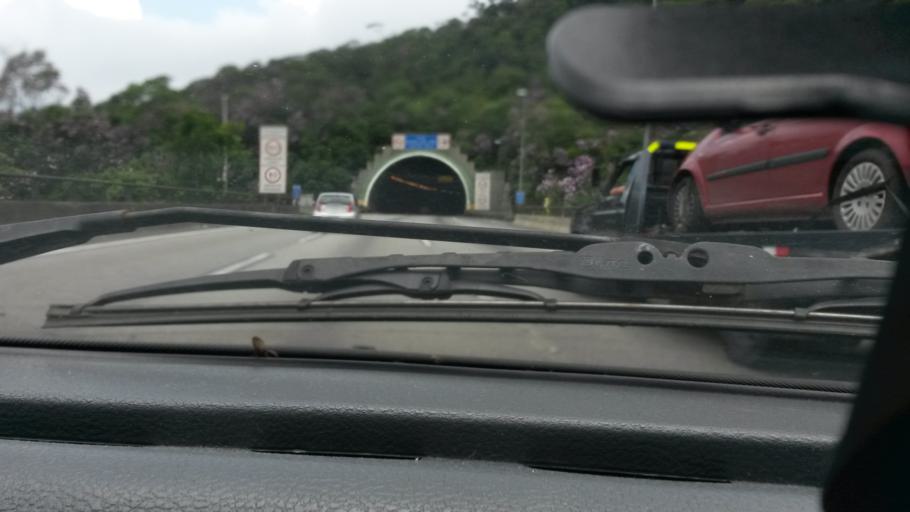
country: BR
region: Sao Paulo
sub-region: Cubatao
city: Cubatao
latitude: -23.9157
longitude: -46.5216
